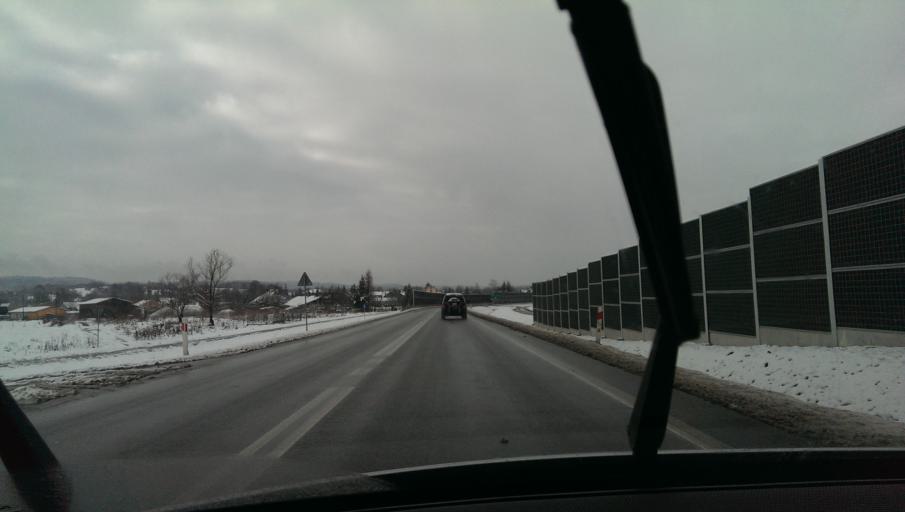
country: PL
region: Subcarpathian Voivodeship
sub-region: Powiat brzozowski
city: Brzozow
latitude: 49.7034
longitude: 22.0287
